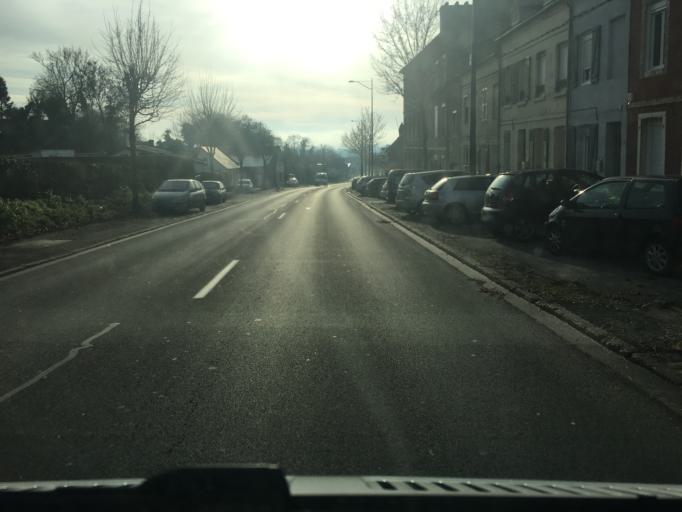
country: FR
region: Picardie
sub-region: Departement de la Somme
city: Abbeville
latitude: 50.1214
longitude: 1.8298
